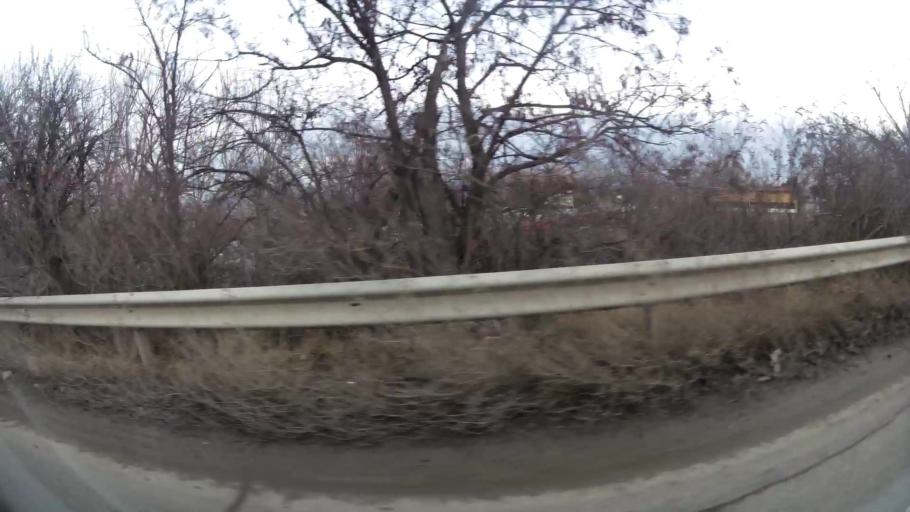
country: BG
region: Sofia-Capital
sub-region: Stolichna Obshtina
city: Sofia
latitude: 42.7504
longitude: 23.2765
